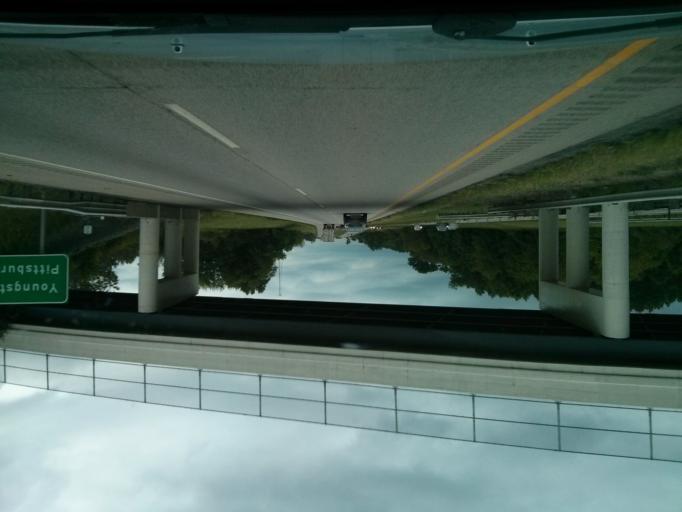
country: US
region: Ohio
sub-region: Mahoning County
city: Craig Beach
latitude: 41.1041
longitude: -81.0325
